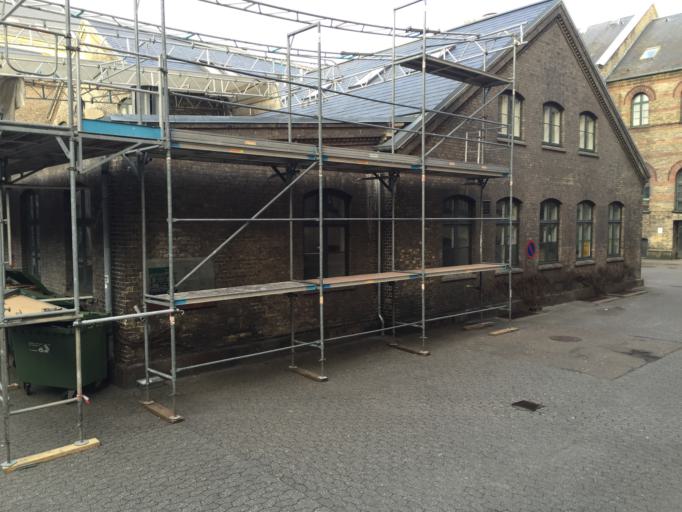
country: DK
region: Capital Region
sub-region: Kobenhavn
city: Copenhagen
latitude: 55.6879
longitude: 12.5689
